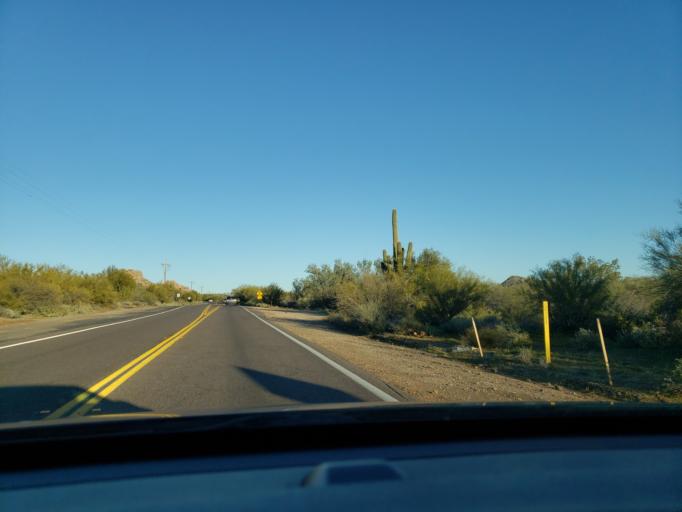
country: US
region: Arizona
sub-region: Maricopa County
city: Carefree
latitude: 33.7992
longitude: -111.9404
